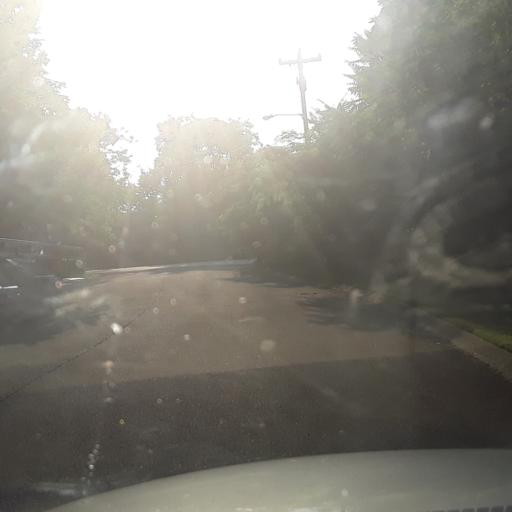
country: US
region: Tennessee
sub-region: Williamson County
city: Brentwood Estates
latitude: 36.0368
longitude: -86.7313
